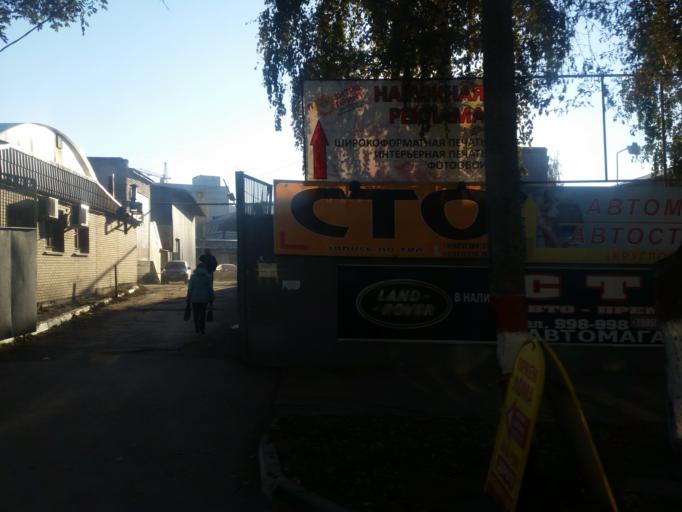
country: RU
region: Ulyanovsk
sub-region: Ulyanovskiy Rayon
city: Ulyanovsk
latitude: 54.3232
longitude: 48.3935
